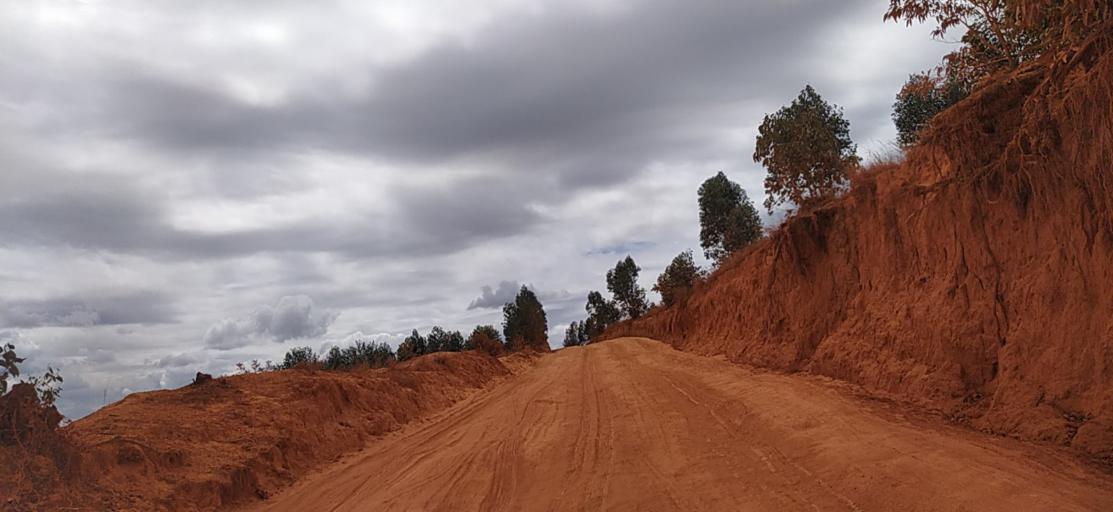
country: MG
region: Alaotra Mangoro
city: Ambatondrazaka
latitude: -18.0481
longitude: 48.2495
